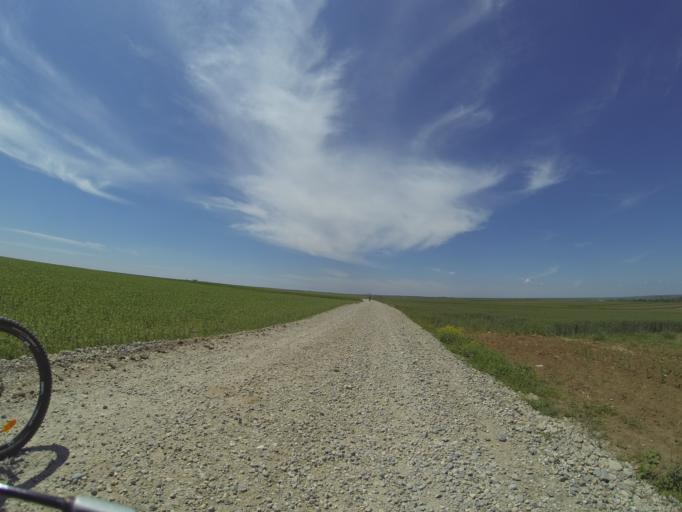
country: RO
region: Dolj
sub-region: Comuna Teslui
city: Teslui
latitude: 44.1898
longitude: 24.1609
